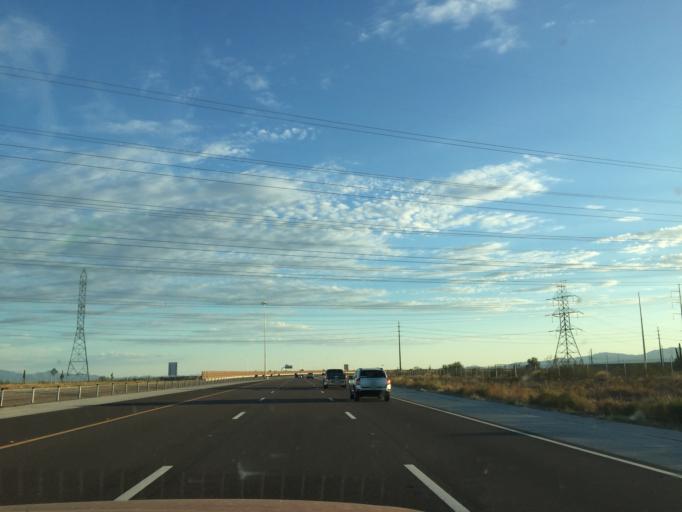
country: US
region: Arizona
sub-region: Maricopa County
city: Sun City West
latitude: 33.7070
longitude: -112.3138
